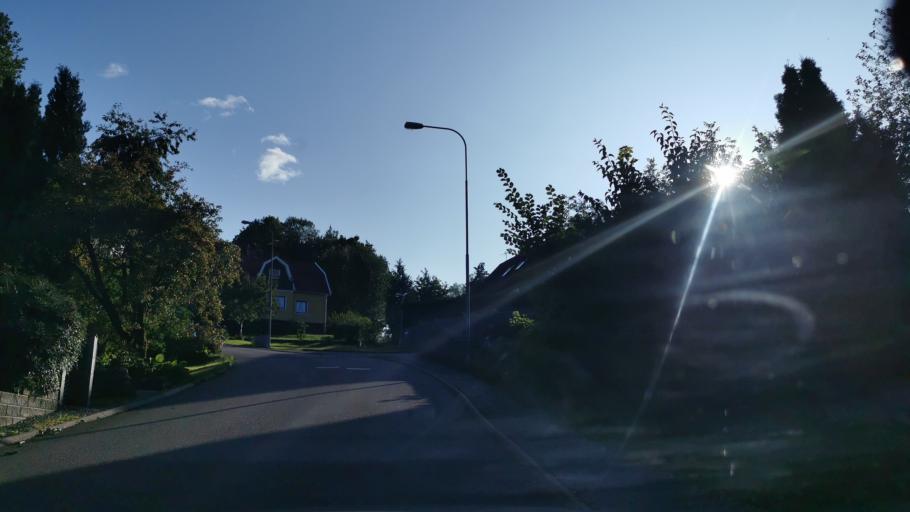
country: SE
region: Vaestra Goetaland
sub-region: Partille Kommun
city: Partille
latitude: 57.7267
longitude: 12.0674
